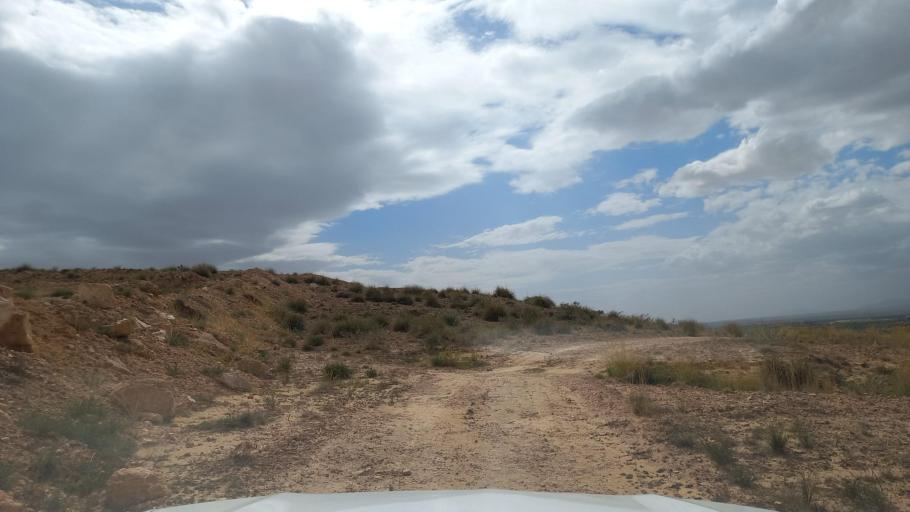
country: TN
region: Al Qasrayn
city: Sbiba
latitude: 35.3574
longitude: 9.1130
